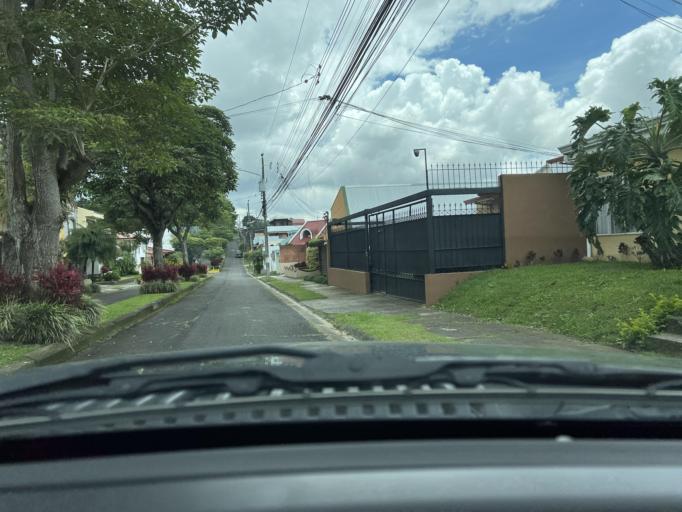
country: CR
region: San Jose
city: Granadilla
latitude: 9.9425
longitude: -84.0216
